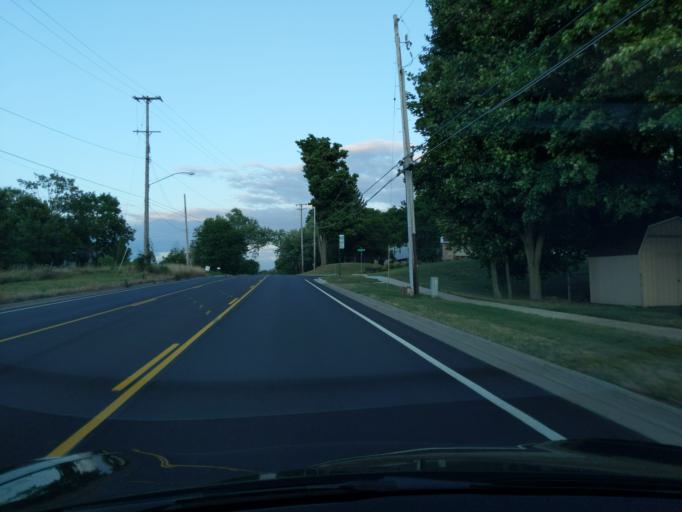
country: US
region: Michigan
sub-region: Ingham County
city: Holt
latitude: 42.6692
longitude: -84.5288
